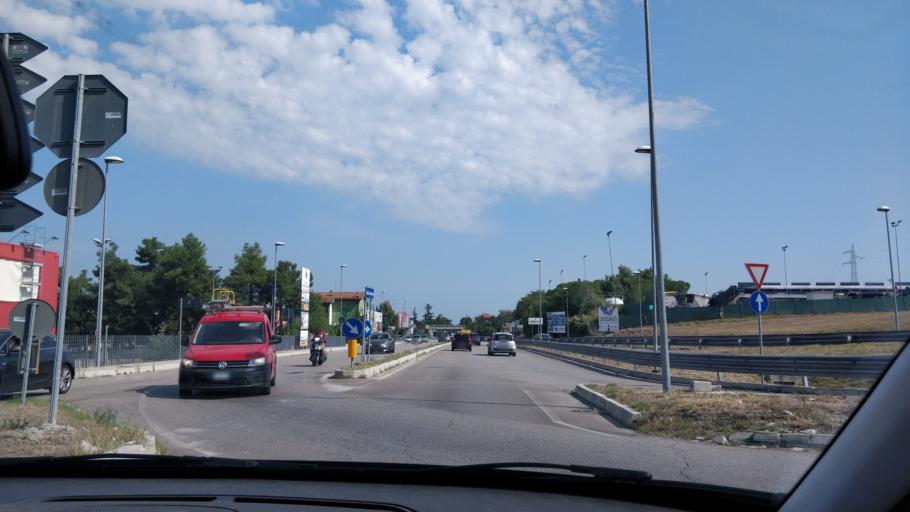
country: IT
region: Abruzzo
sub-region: Provincia di Chieti
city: Chieti
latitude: 42.3953
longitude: 14.1629
